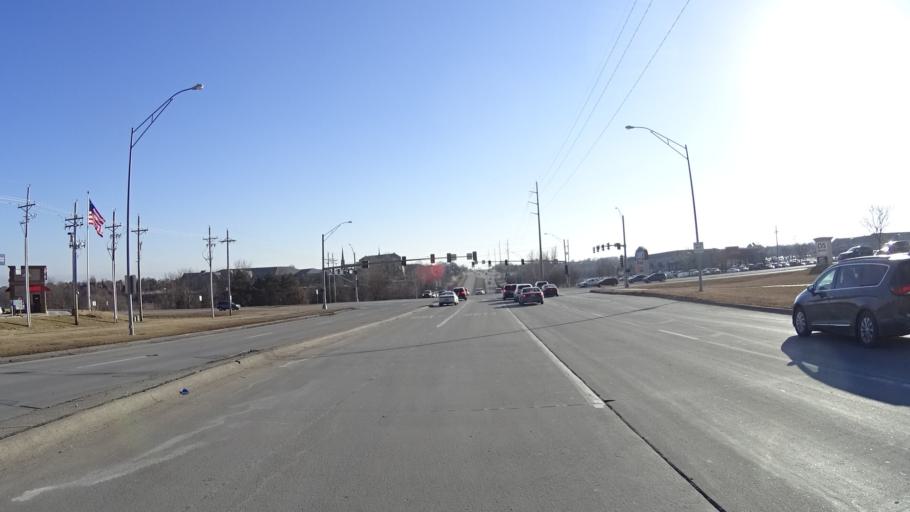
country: US
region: Nebraska
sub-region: Douglas County
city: Bennington
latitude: 41.2931
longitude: -96.1390
